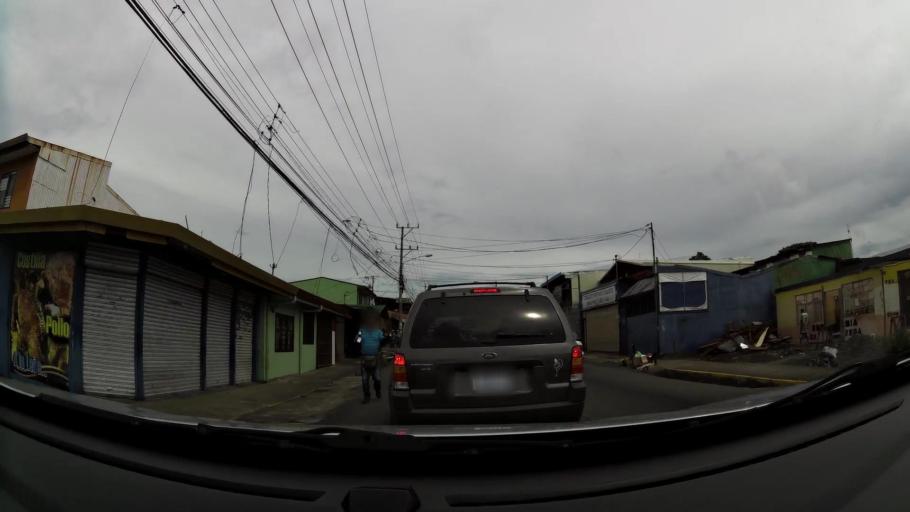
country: CR
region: San Jose
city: Curridabat
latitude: 9.9139
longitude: -84.0359
